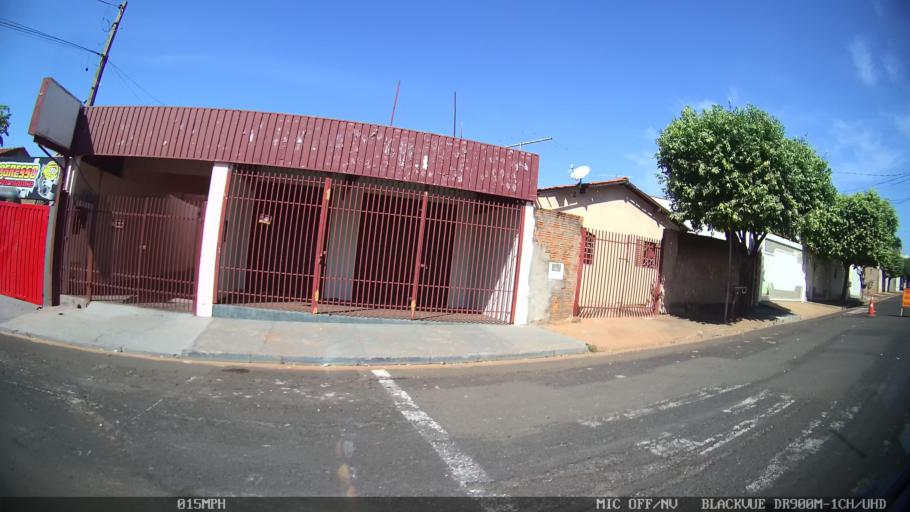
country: BR
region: Sao Paulo
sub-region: Sao Jose Do Rio Preto
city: Sao Jose do Rio Preto
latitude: -20.7762
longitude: -49.4033
